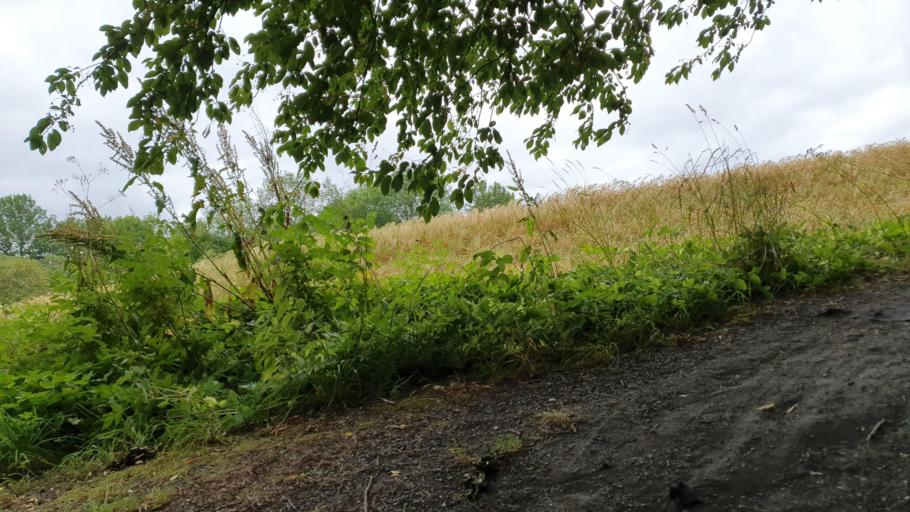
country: NO
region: Sor-Trondelag
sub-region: Rissa
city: Rissa
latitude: 63.4955
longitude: 10.0107
